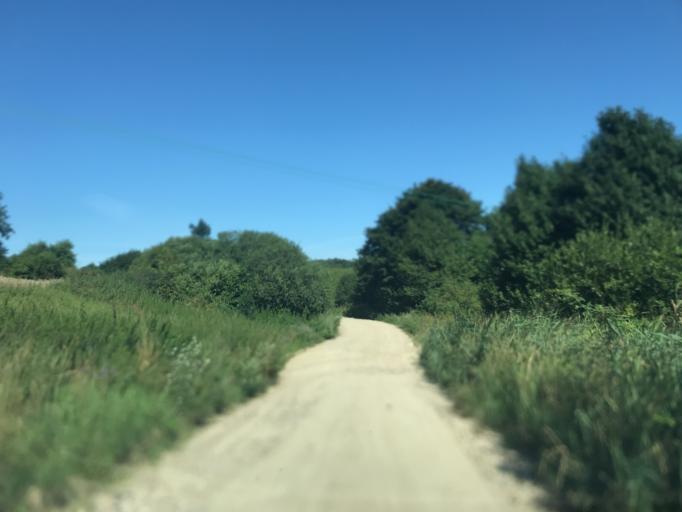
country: PL
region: Warmian-Masurian Voivodeship
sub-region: Powiat ilawski
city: Lubawa
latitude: 53.5337
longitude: 19.8954
